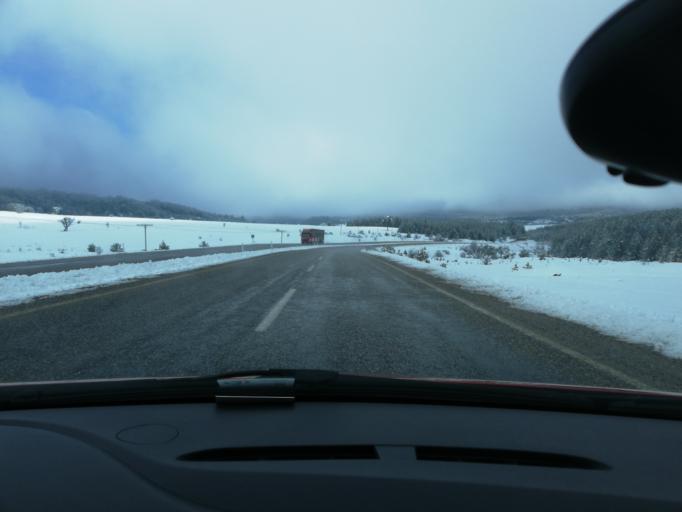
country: TR
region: Kastamonu
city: Ihsangazi
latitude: 41.3035
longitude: 33.5597
